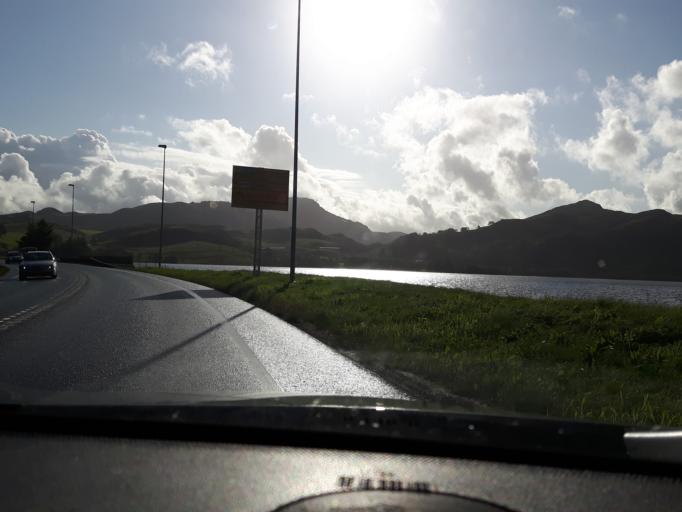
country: NO
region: Rogaland
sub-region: Gjesdal
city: Algard
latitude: 58.7654
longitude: 5.8747
